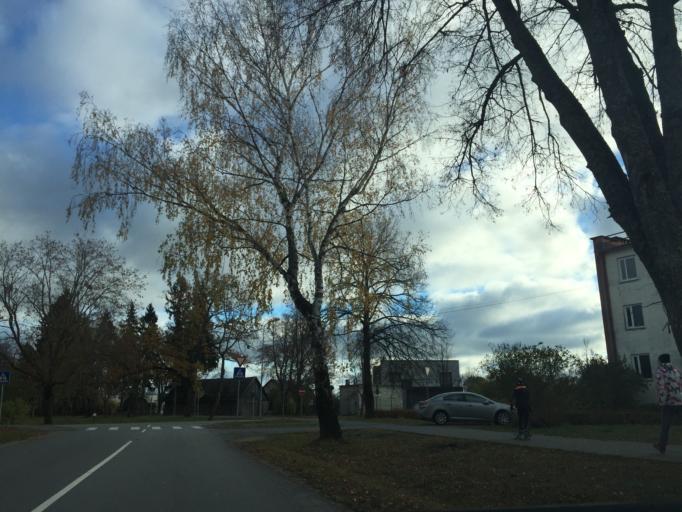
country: LV
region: Carnikava
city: Carnikava
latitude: 57.1311
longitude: 24.2671
